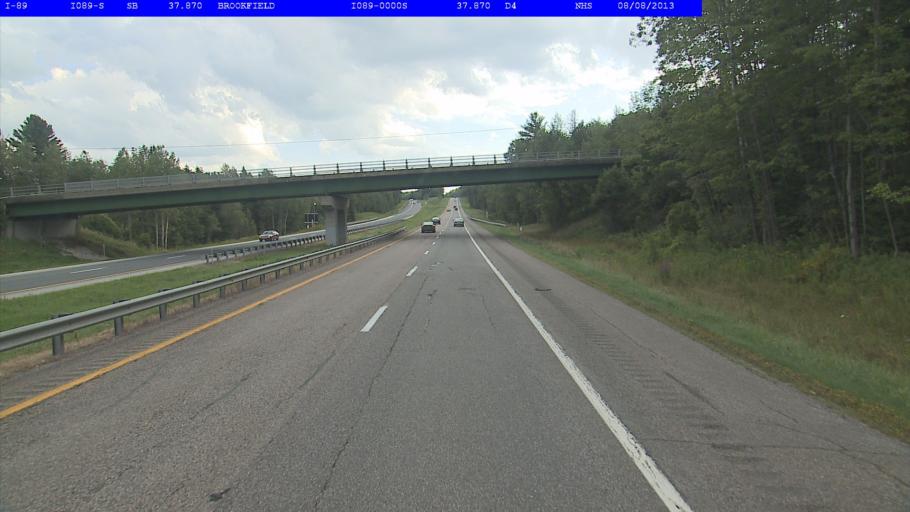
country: US
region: Vermont
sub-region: Orange County
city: Williamstown
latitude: 44.0442
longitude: -72.6092
